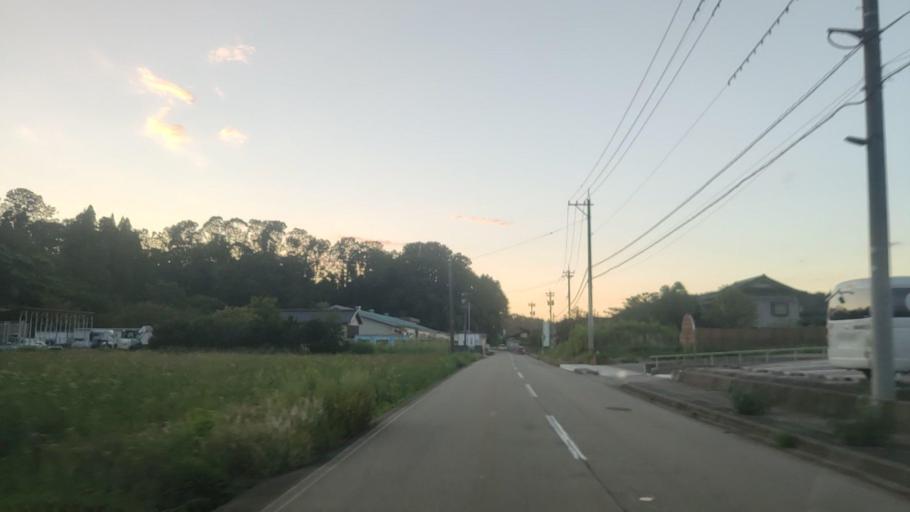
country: JP
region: Ishikawa
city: Tsubata
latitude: 36.6634
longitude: 136.7497
